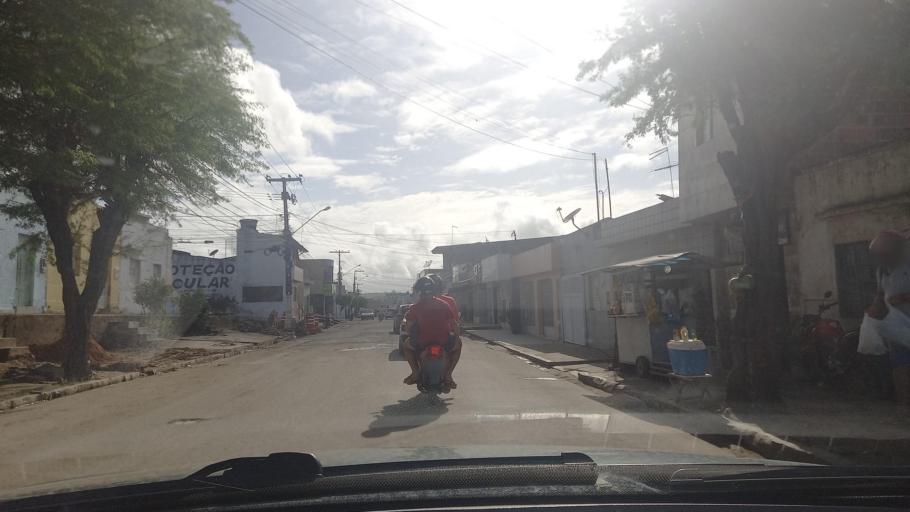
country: BR
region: Pernambuco
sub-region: Vitoria De Santo Antao
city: Vitoria de Santo Antao
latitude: -8.1085
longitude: -35.2855
